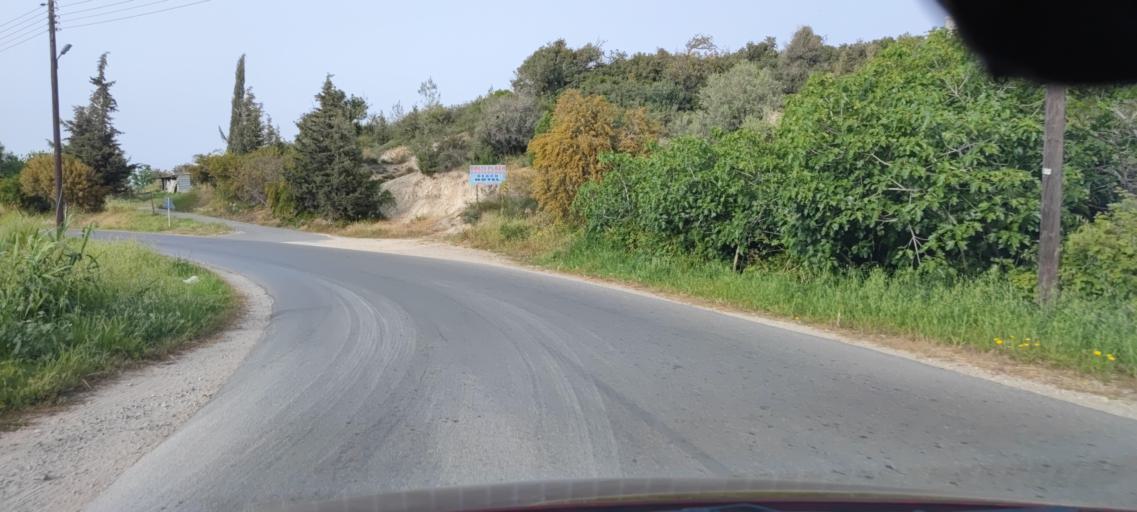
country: CY
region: Ammochostos
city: Leonarisso
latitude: 35.5369
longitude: 34.1931
